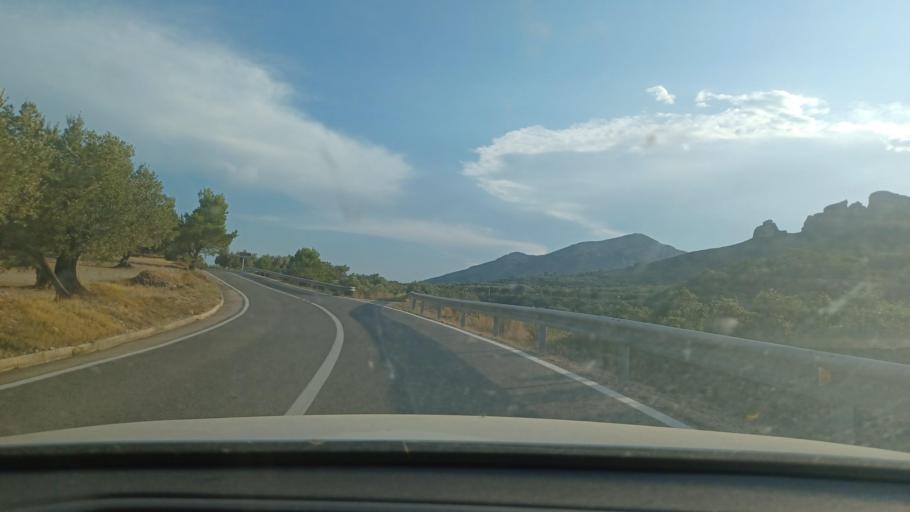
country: ES
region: Catalonia
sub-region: Provincia de Tarragona
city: Mas de Barberans
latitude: 40.7286
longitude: 0.3723
